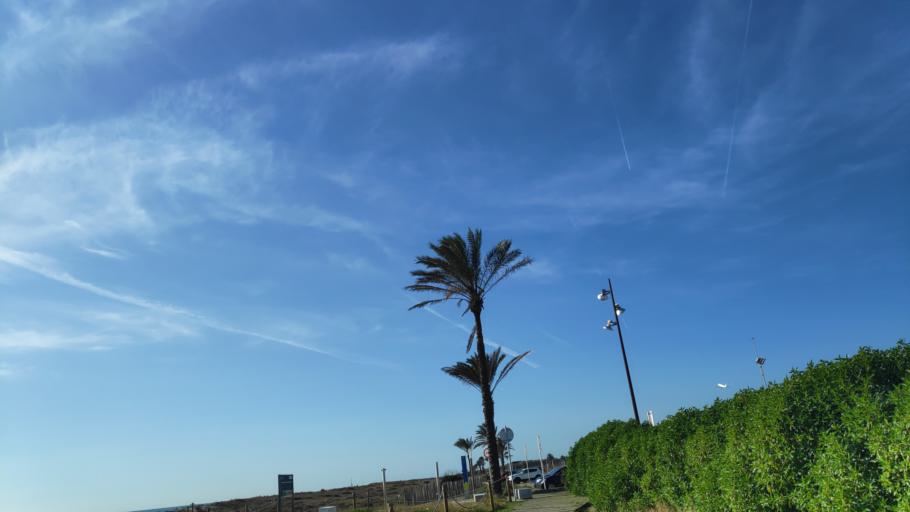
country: ES
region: Catalonia
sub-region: Provincia de Barcelona
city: El Prat de Llobregat
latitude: 41.2838
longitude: 2.0946
